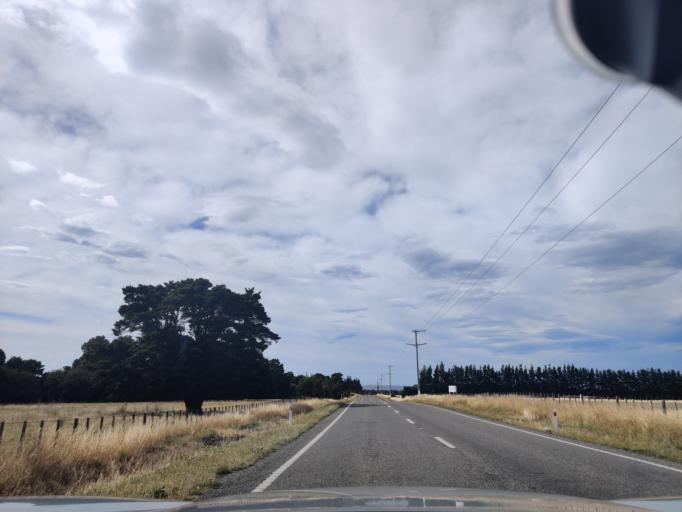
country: NZ
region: Wellington
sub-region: Masterton District
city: Masterton
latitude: -40.8365
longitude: 175.6294
